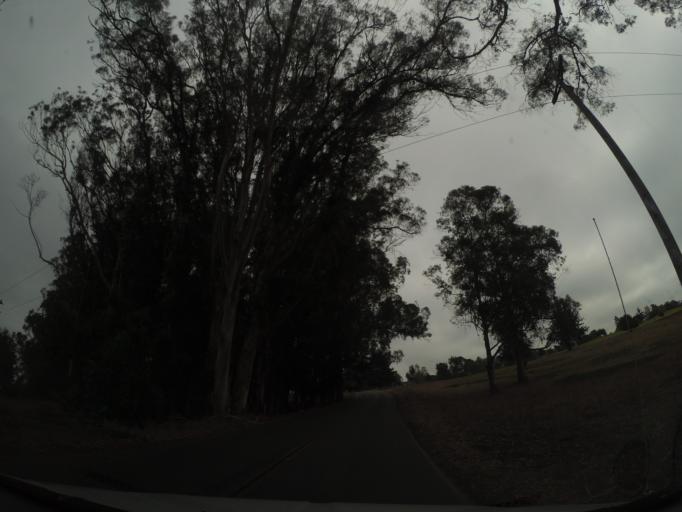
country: US
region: California
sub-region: San Luis Obispo County
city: Morro Bay
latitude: 35.3499
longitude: -120.8434
